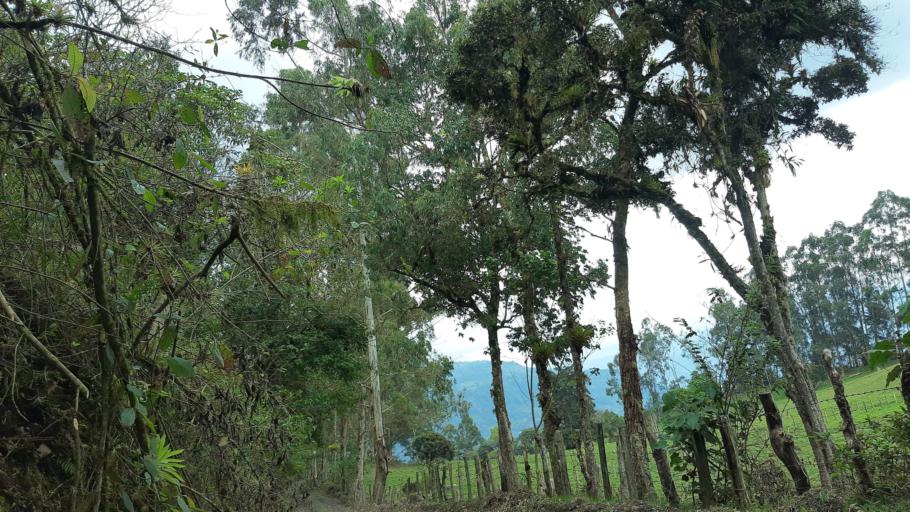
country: CO
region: Boyaca
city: Garagoa
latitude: 5.0544
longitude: -73.3486
